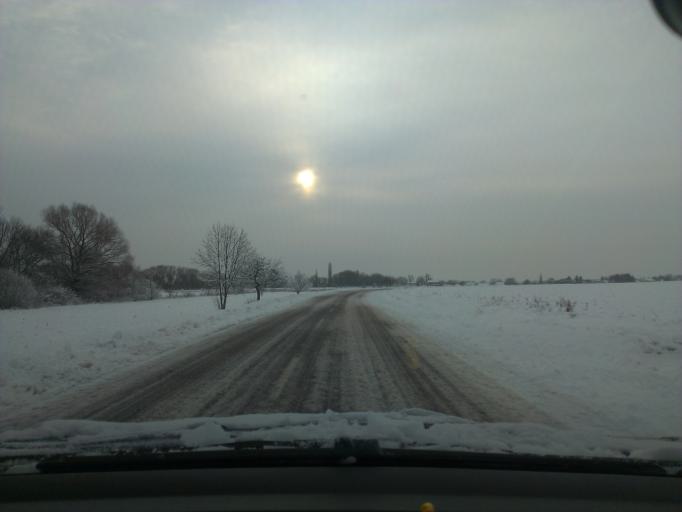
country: SK
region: Trnavsky
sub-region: Okres Trnava
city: Piestany
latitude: 48.5345
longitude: 17.9574
